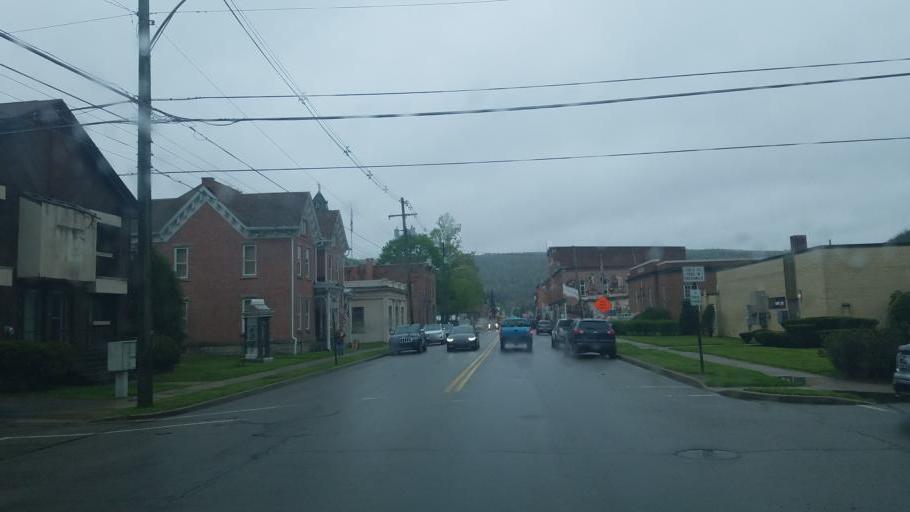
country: US
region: Pennsylvania
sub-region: Potter County
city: Coudersport
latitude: 41.7765
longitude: -78.0208
